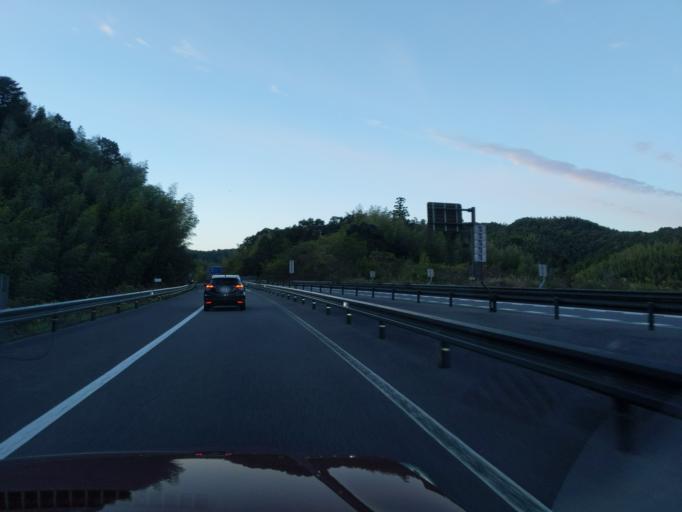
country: JP
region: Tokushima
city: Anan
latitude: 33.7989
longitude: 134.5929
